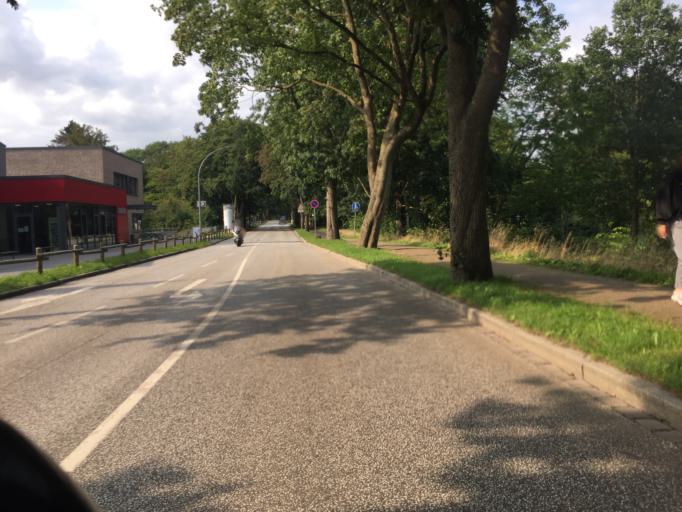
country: DE
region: Schleswig-Holstein
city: Itzehoe
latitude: 53.9308
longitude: 9.5130
